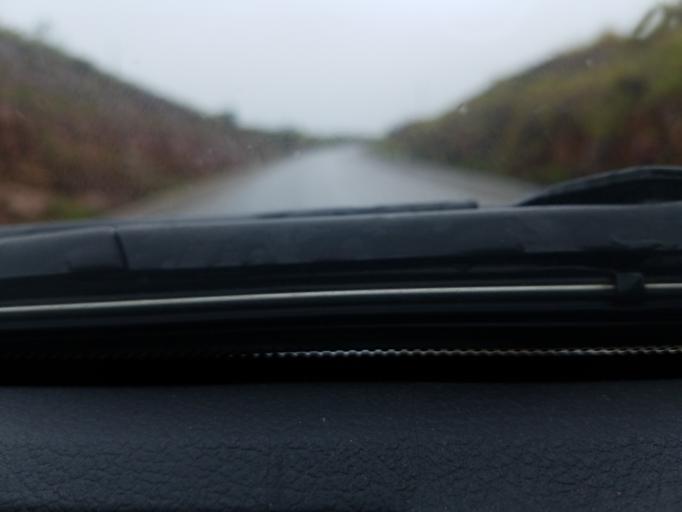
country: TZ
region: Kigoma
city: Mwandiga
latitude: -4.6648
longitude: 29.7250
